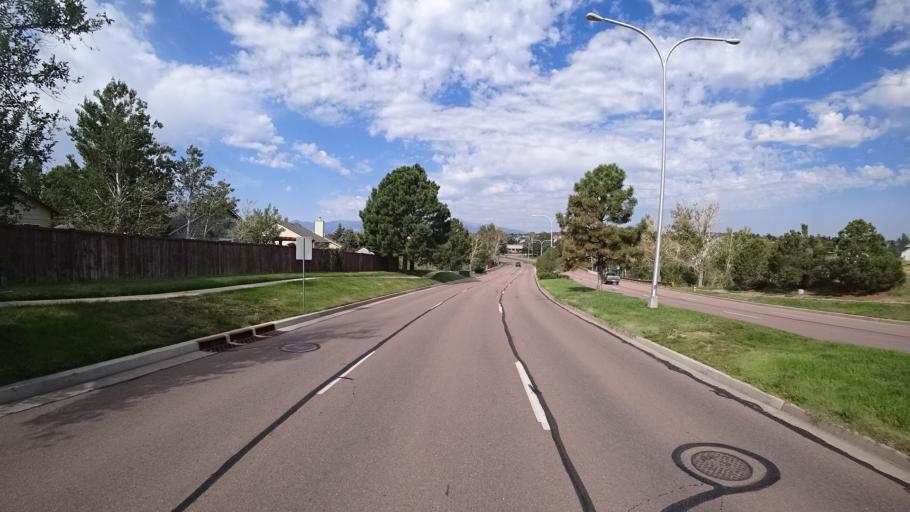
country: US
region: Colorado
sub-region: El Paso County
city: Cimarron Hills
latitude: 38.8986
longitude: -104.7056
